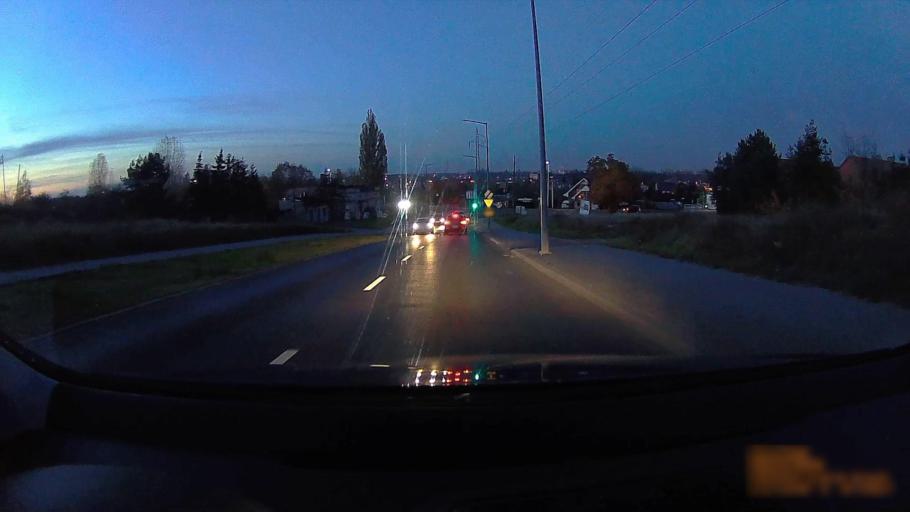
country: PL
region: Greater Poland Voivodeship
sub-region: Konin
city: Konin
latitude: 52.2023
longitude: 18.2332
